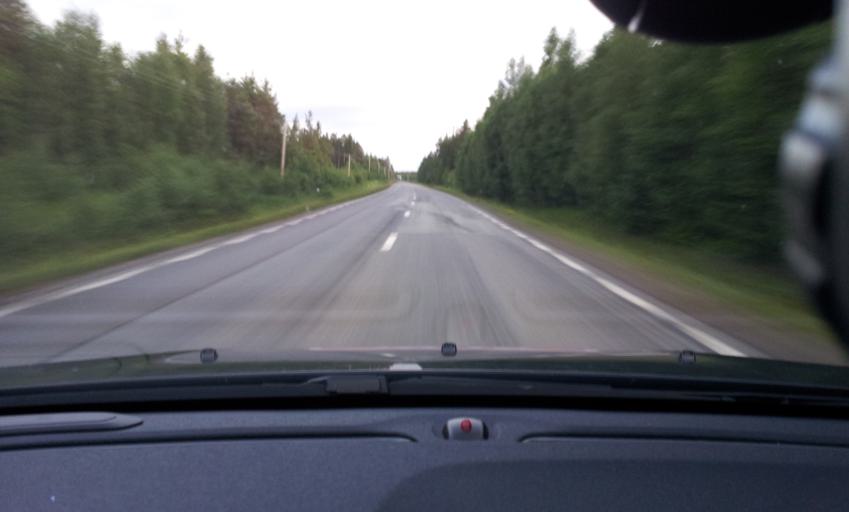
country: SE
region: Jaemtland
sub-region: Ragunda Kommun
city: Hammarstrand
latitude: 63.0086
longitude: 16.1179
